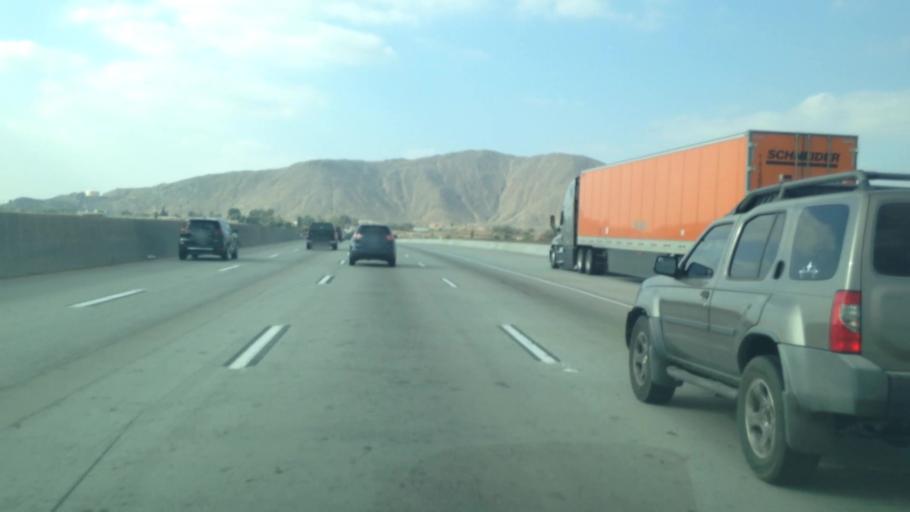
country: US
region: California
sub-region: Riverside County
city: Rubidoux
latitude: 34.0034
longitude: -117.3811
